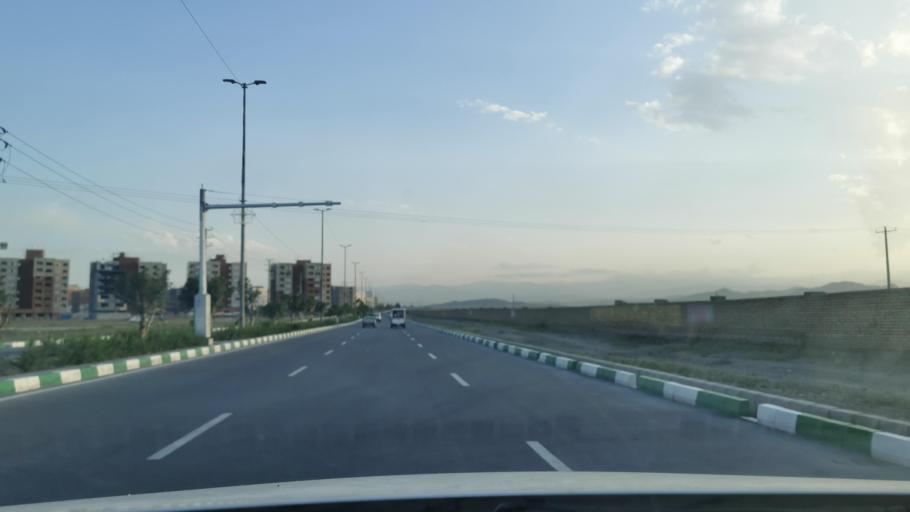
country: IR
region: Razavi Khorasan
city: Mashhad
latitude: 36.3966
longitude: 59.4749
